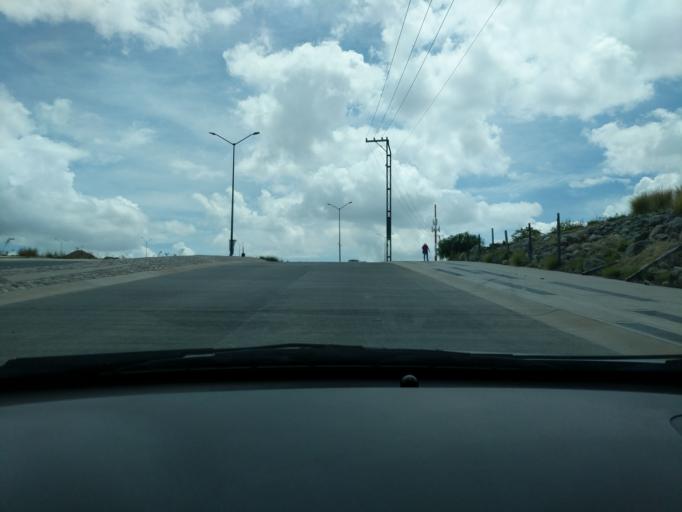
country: MX
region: San Luis Potosi
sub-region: Mexquitic de Carmona
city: Guadalupe Victoria
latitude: 22.1635
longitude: -101.0463
